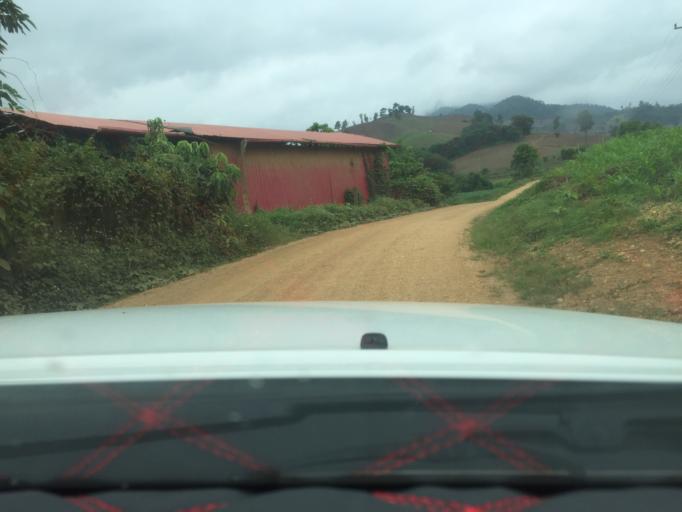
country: TH
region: Phayao
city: Phu Sang
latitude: 19.6972
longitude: 100.4963
